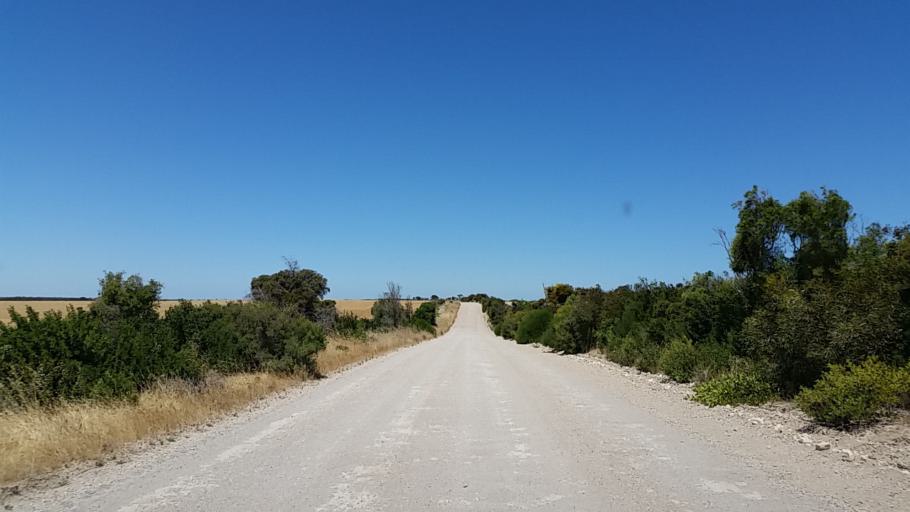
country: AU
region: South Australia
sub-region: Yorke Peninsula
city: Honiton
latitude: -35.0914
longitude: 137.4543
